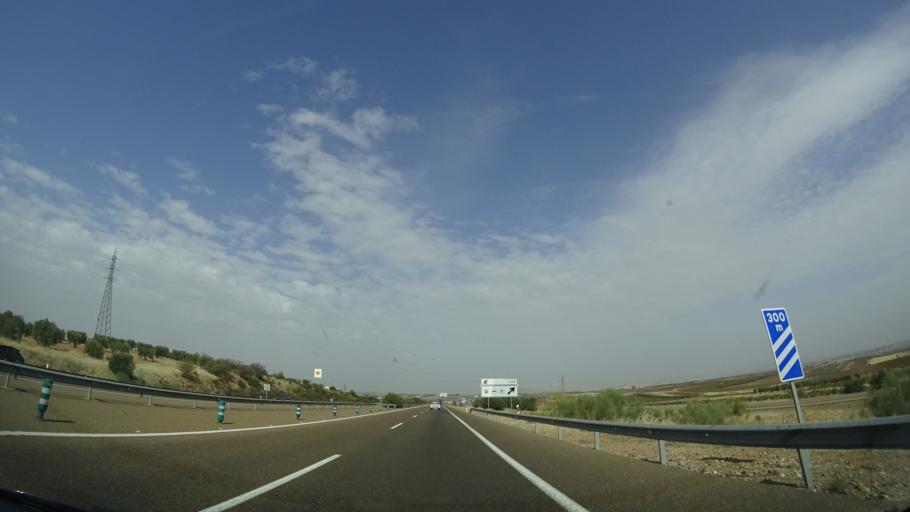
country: ES
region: Extremadura
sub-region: Provincia de Badajoz
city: Calamonte
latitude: 38.8551
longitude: -6.3620
